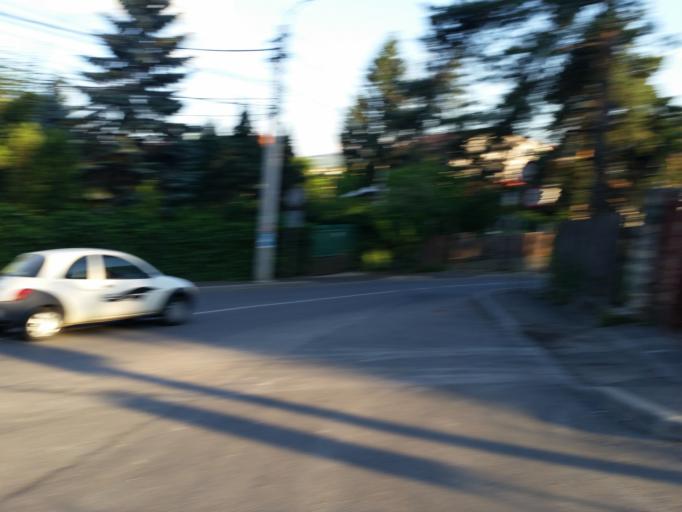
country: RO
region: Cluj
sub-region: Municipiul Cluj-Napoca
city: Cluj-Napoca
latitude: 46.7761
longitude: 23.5712
